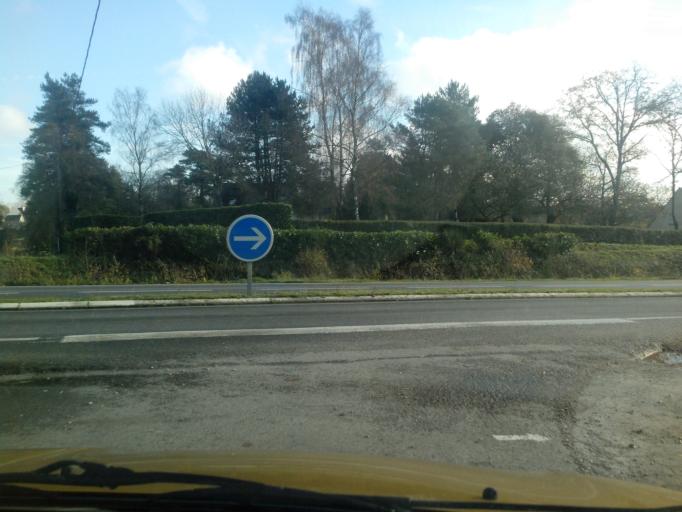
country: FR
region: Brittany
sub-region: Departement du Morbihan
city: Molac
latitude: 47.7298
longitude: -2.4421
